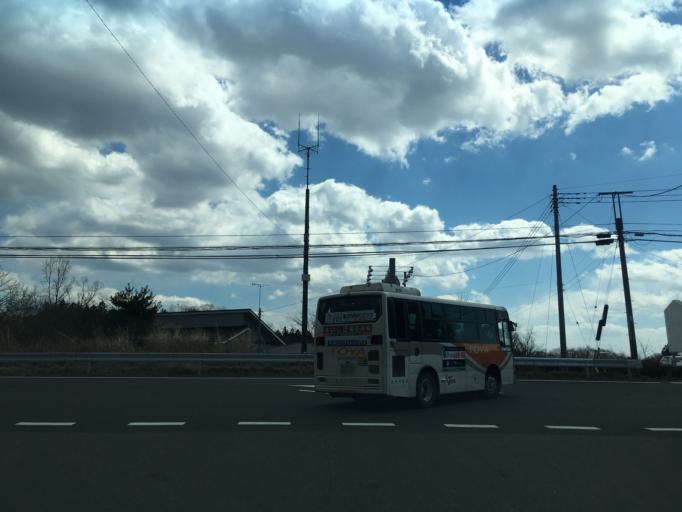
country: JP
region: Tochigi
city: Kuroiso
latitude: 37.0459
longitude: 140.0248
